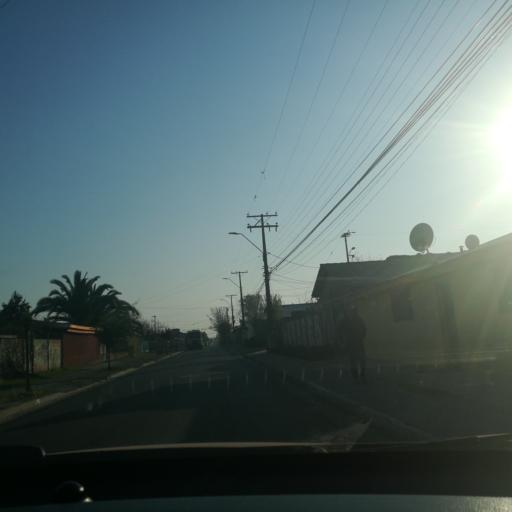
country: CL
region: O'Higgins
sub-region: Provincia de Cachapoal
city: Rancagua
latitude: -34.1716
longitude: -70.7124
